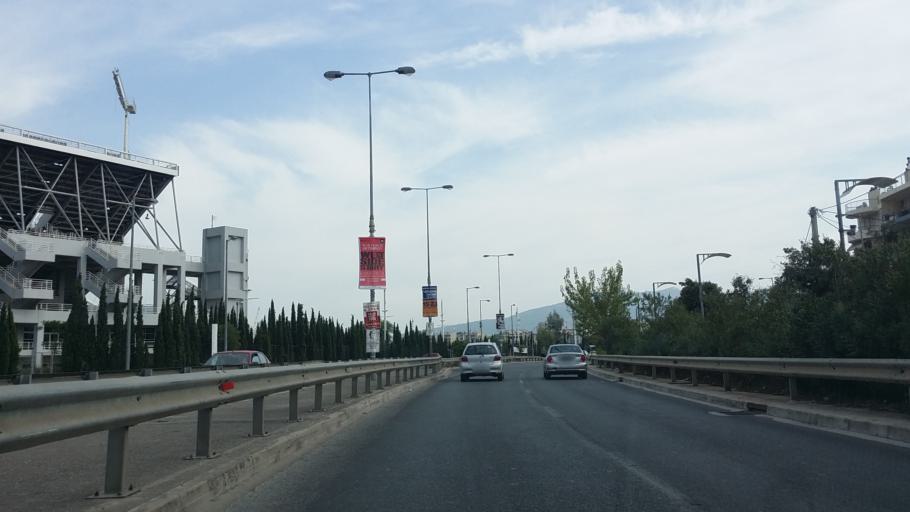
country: GR
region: Attica
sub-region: Nomarchia Athinas
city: Filothei
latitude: 38.0385
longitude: 23.7793
